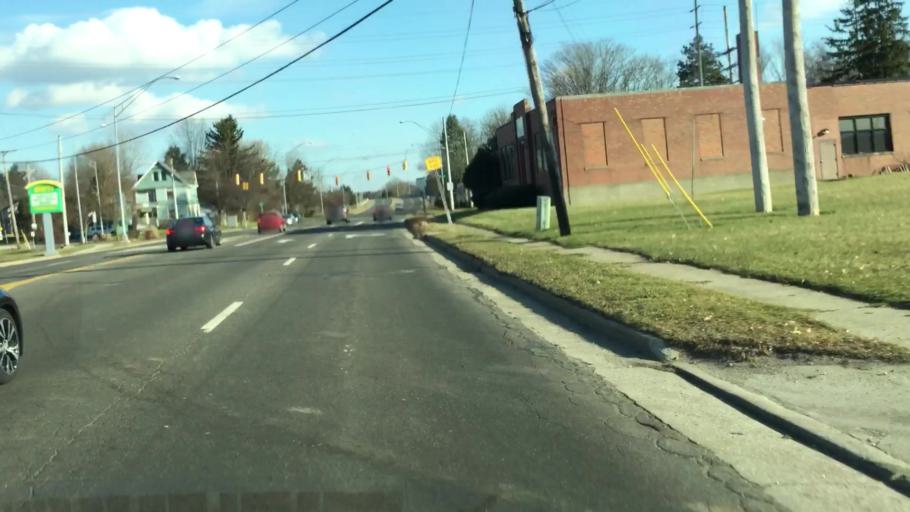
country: US
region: Ohio
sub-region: Portage County
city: Kent
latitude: 41.1513
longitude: -81.3786
